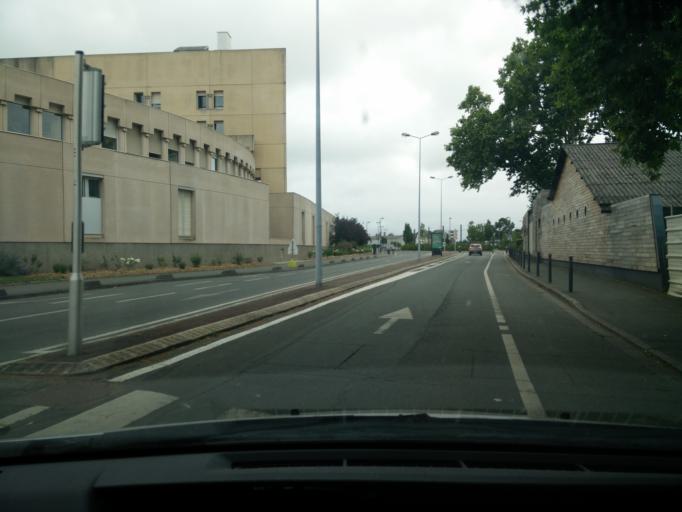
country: FR
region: Pays de la Loire
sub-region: Departement de Maine-et-Loire
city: Angers
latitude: 47.4795
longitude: -0.5554
